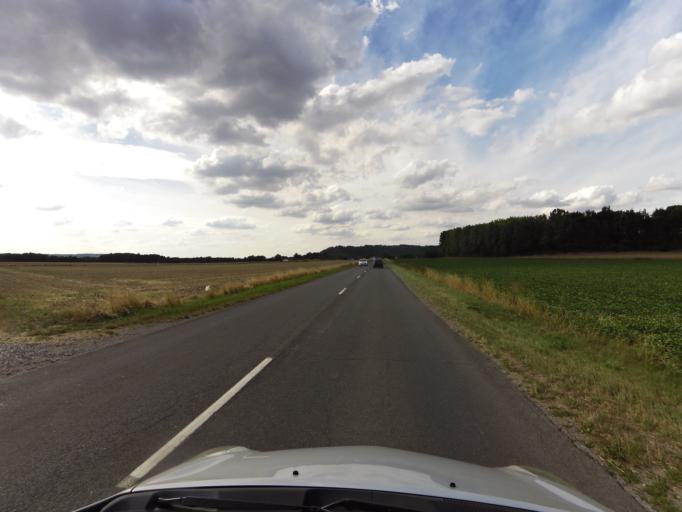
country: FR
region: Picardie
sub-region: Departement de l'Aisne
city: Bruyeres-et-Montberault
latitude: 49.5406
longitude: 3.6398
